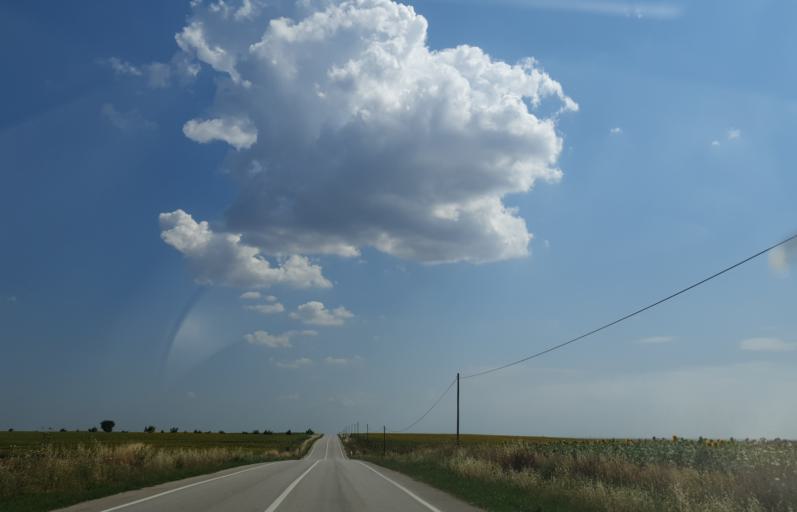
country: TR
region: Kirklareli
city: Buyukkaristiran
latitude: 41.4313
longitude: 27.5824
